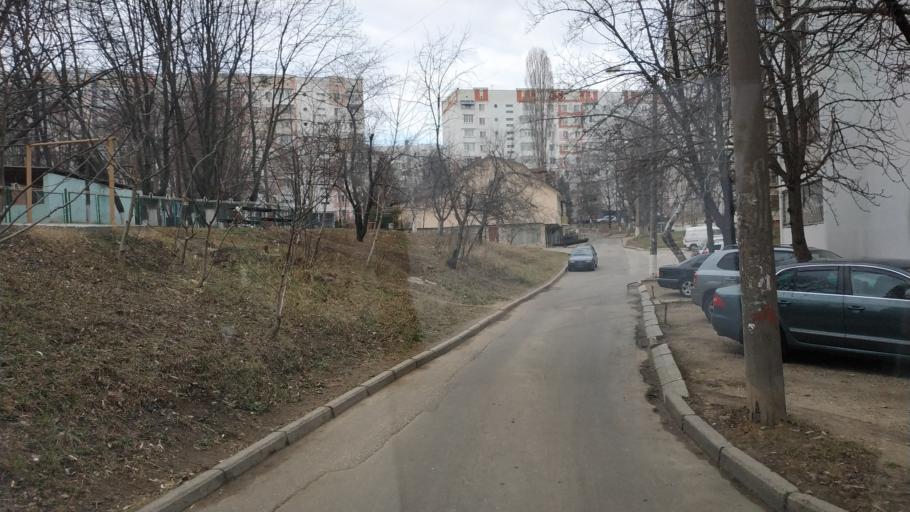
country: MD
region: Chisinau
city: Vatra
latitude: 47.0397
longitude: 28.7721
